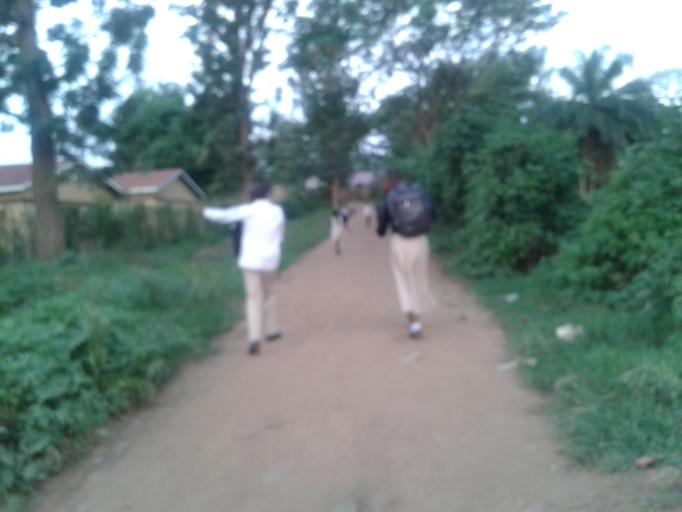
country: UG
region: Eastern Region
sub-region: Mbale District
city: Mbale
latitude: 1.0813
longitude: 34.1757
